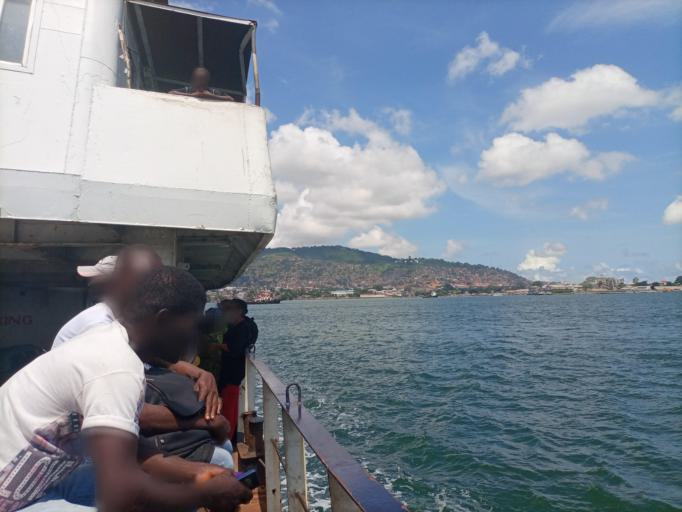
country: SL
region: Western Area
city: Freetown
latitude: 8.4905
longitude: -13.1918
